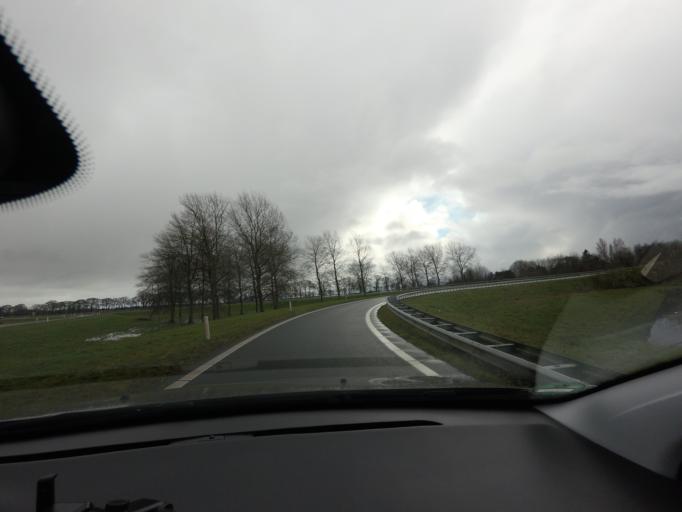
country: NL
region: Groningen
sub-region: Gemeente Veendam
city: Veendam
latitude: 53.0430
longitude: 6.8245
